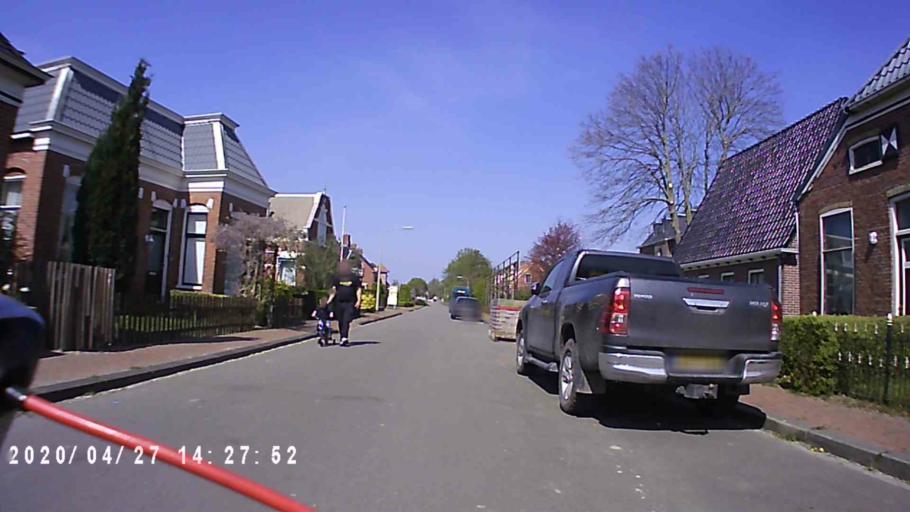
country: NL
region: Groningen
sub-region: Gemeente De Marne
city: Ulrum
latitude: 53.3879
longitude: 6.3927
